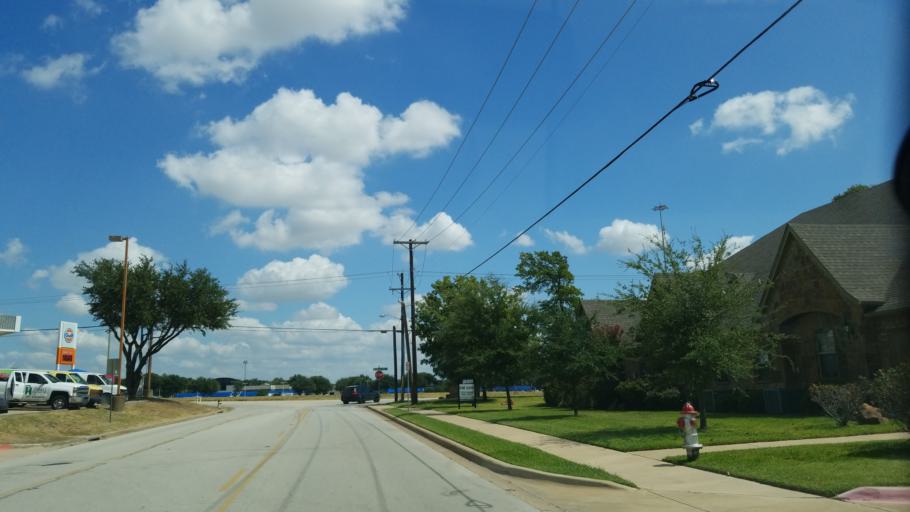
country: US
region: Texas
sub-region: Tarrant County
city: Grapevine
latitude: 32.9091
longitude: -97.1012
